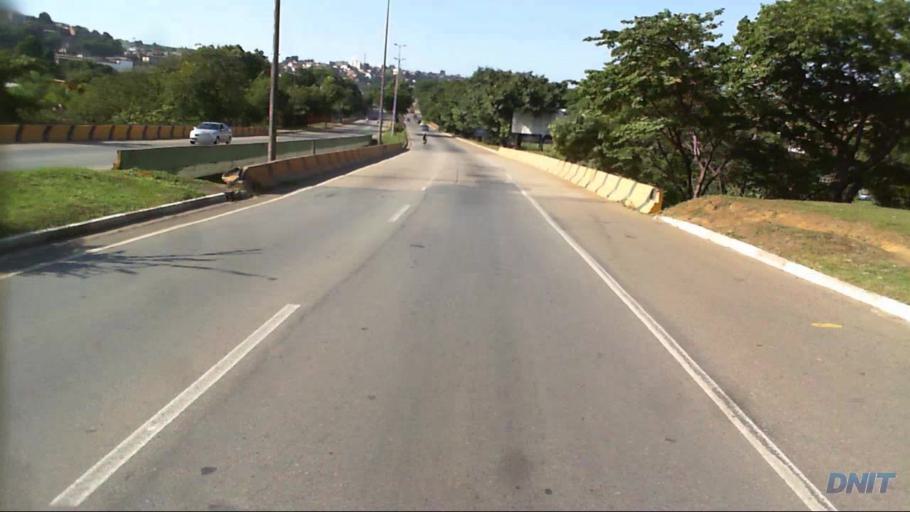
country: BR
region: Minas Gerais
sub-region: Ipatinga
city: Ipatinga
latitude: -19.4702
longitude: -42.5384
